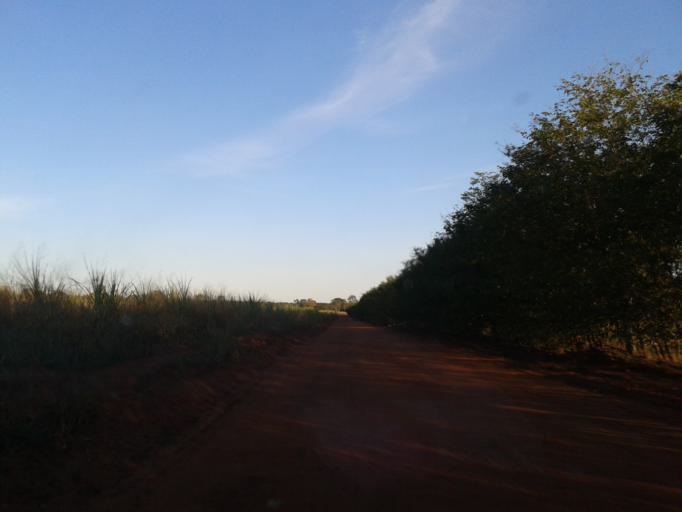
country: BR
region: Minas Gerais
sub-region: Santa Vitoria
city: Santa Vitoria
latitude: -19.0239
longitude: -50.3656
